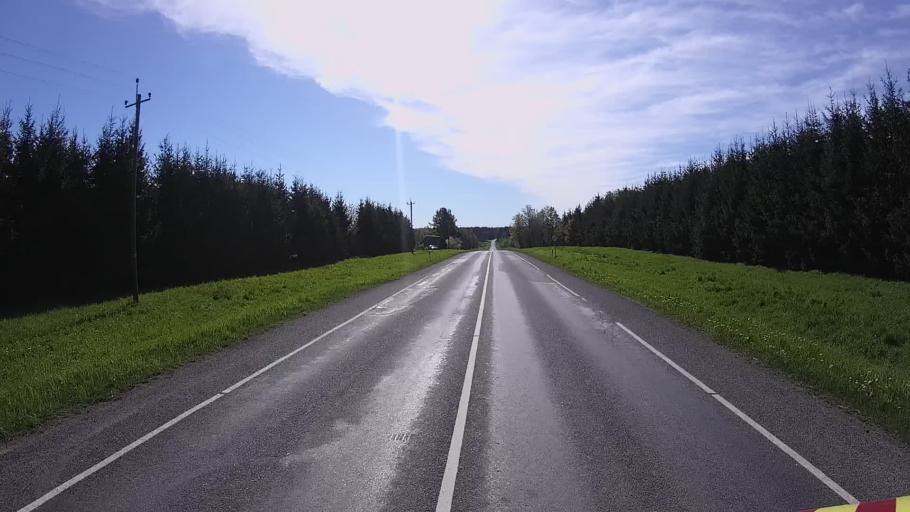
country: EE
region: Polvamaa
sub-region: Polva linn
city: Polva
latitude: 58.1899
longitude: 27.0875
